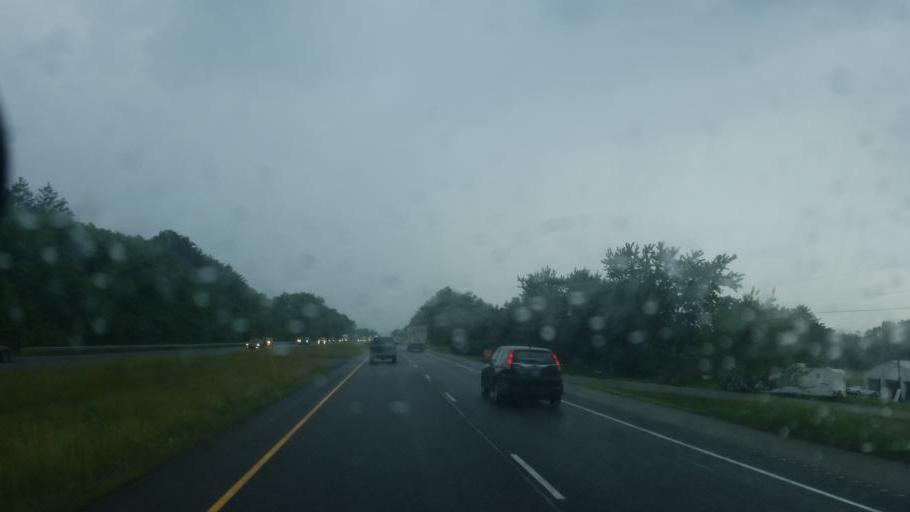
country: US
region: Indiana
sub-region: Whitley County
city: Columbia City
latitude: 41.1289
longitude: -85.3863
